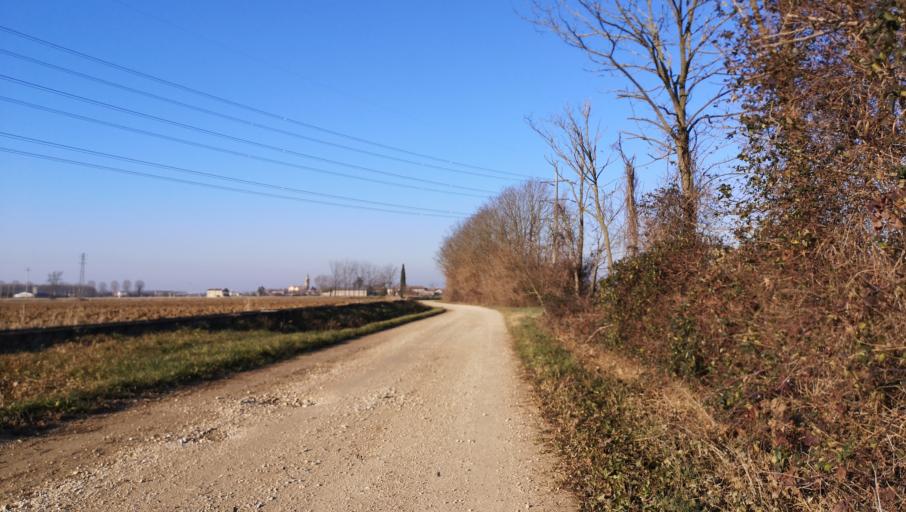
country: IT
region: Friuli Venezia Giulia
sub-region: Provincia di Udine
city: Santa Maria la Longa
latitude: 45.9539
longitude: 13.2943
